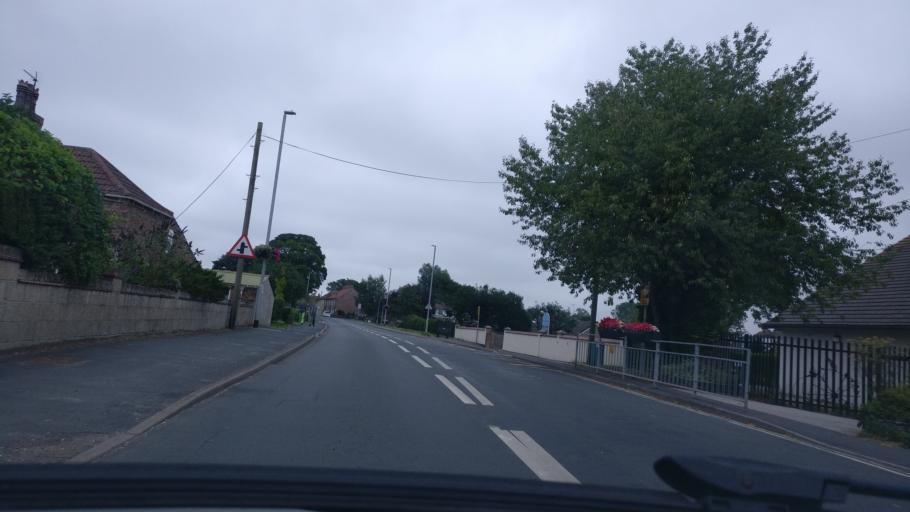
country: GB
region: England
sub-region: East Riding of Yorkshire
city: Leven
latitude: 53.8900
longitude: -0.3163
